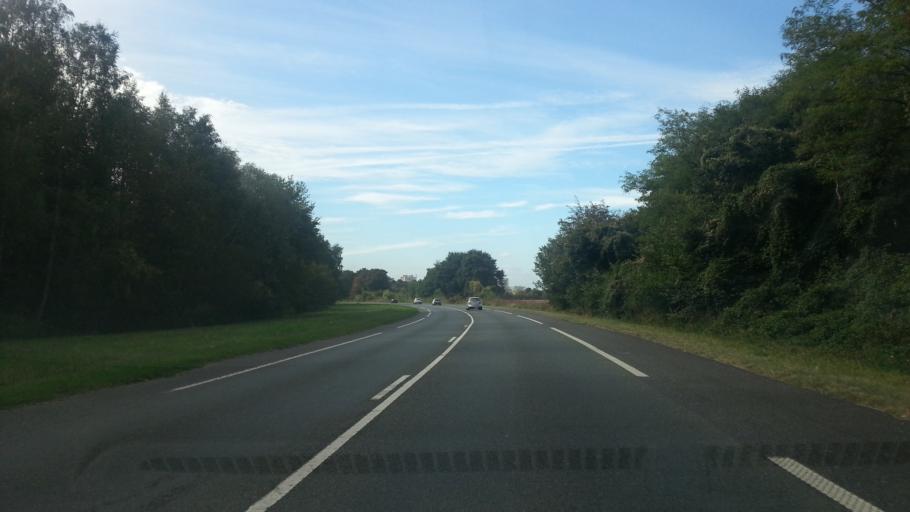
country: FR
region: Picardie
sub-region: Departement de l'Oise
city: Creil
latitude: 49.2451
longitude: 2.4916
